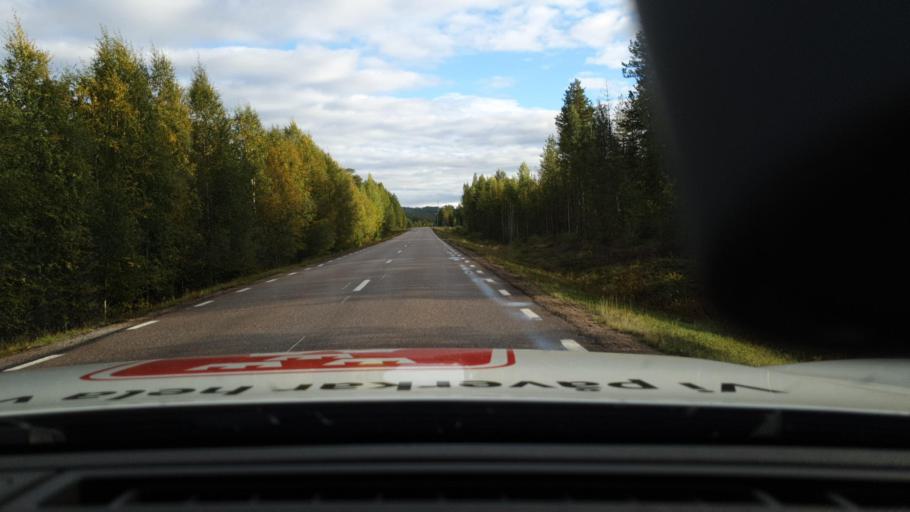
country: SE
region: Norrbotten
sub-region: Overkalix Kommun
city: OEverkalix
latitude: 66.6151
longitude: 22.7531
